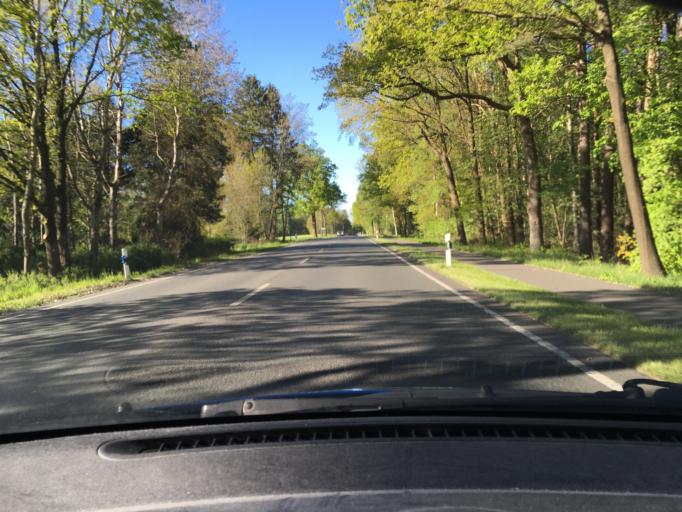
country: DE
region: Lower Saxony
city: Soltau
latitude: 53.0404
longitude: 9.8551
